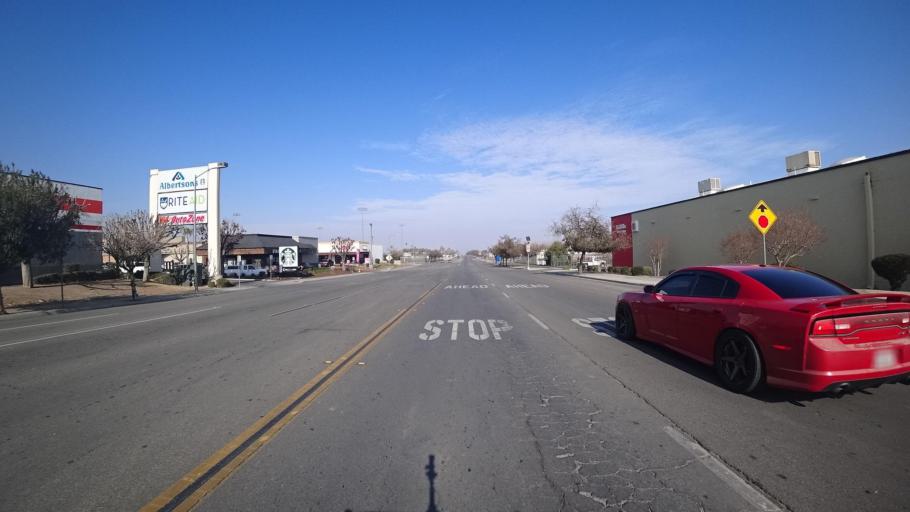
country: US
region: California
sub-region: Kern County
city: Taft
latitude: 35.1453
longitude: -119.4651
